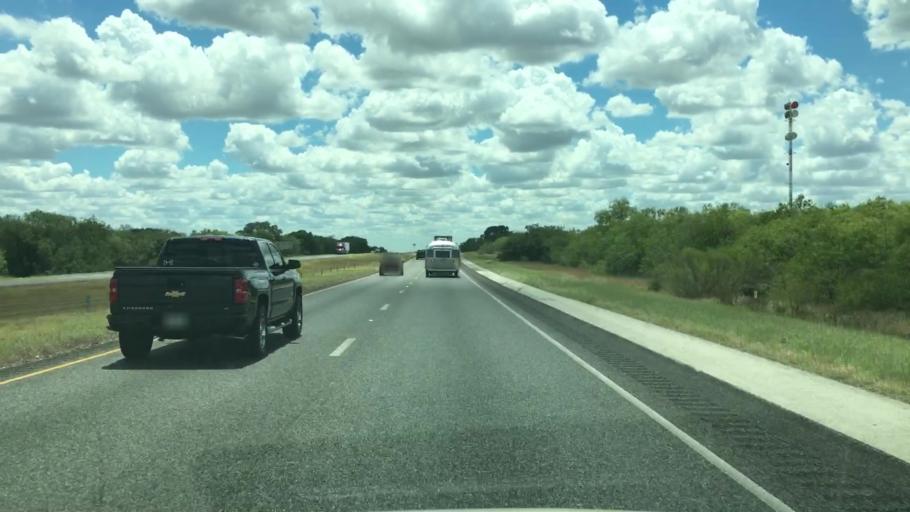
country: US
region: Texas
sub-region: Bexar County
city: Elmendorf
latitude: 29.1310
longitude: -98.4303
